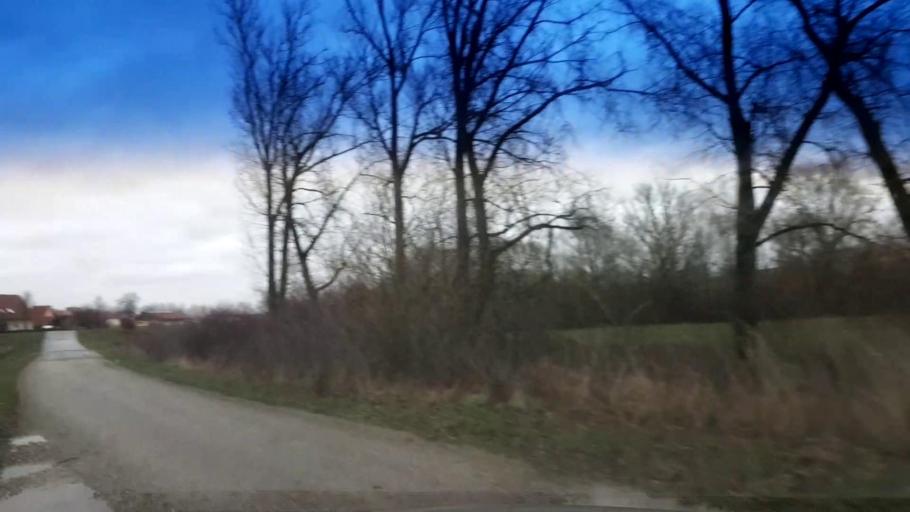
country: DE
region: Bavaria
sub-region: Upper Franconia
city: Rattelsdorf
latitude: 50.0040
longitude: 10.9064
